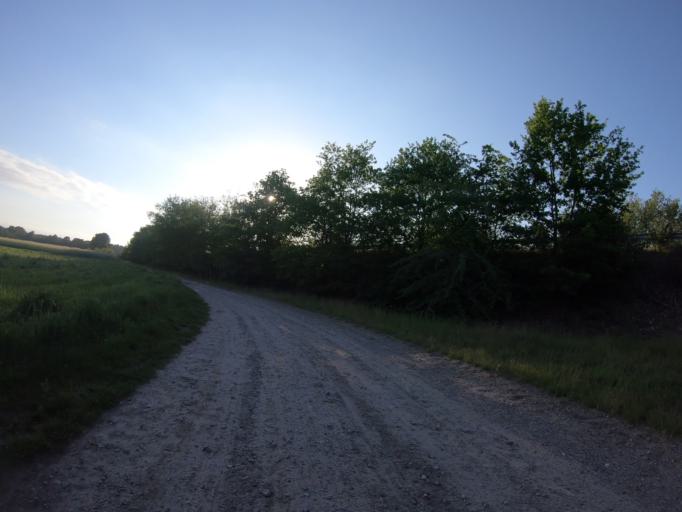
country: DE
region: Lower Saxony
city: Wagenhoff
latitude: 52.5168
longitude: 10.5165
